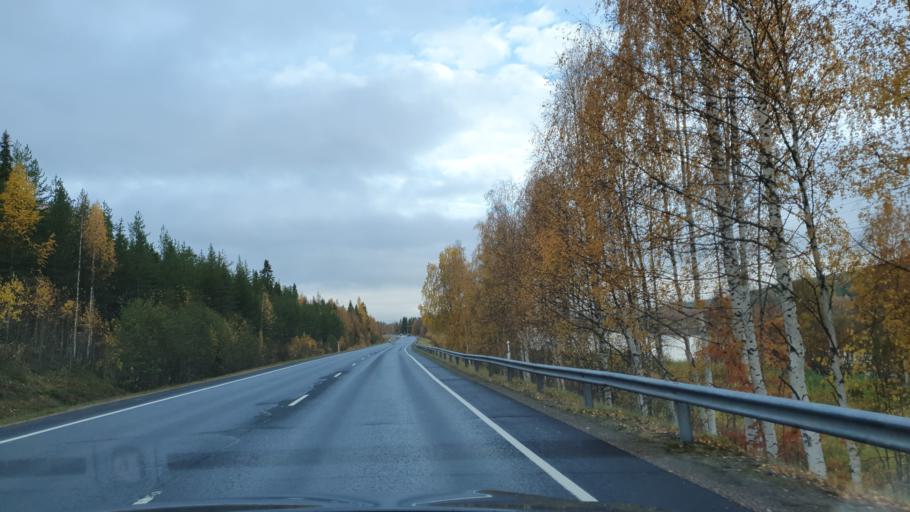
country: FI
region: Lapland
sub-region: Rovaniemi
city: Rovaniemi
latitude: 66.6064
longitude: 25.5752
